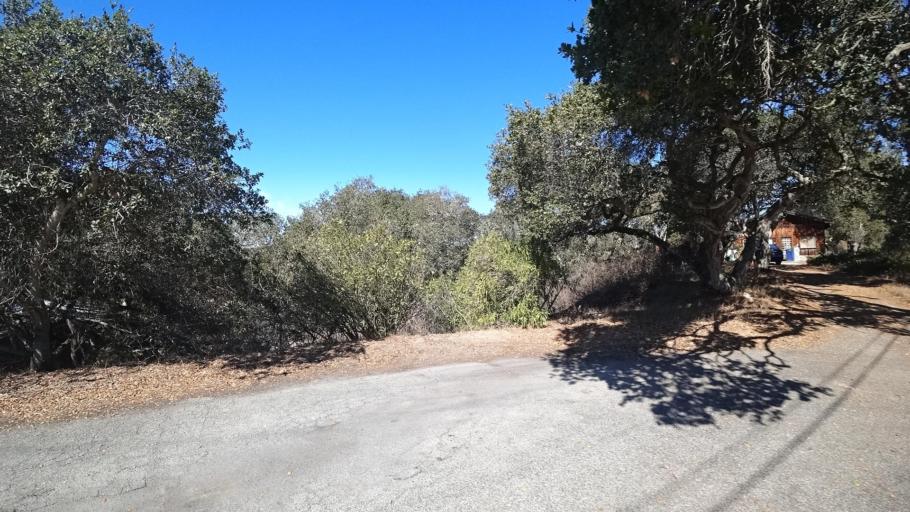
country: US
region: California
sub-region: San Benito County
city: Aromas
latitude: 36.8304
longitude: -121.6314
